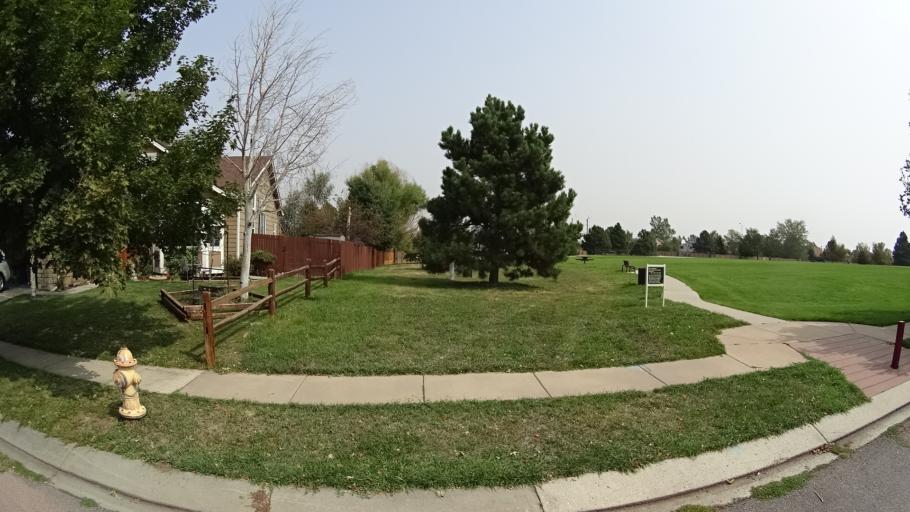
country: US
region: Colorado
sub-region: El Paso County
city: Cimarron Hills
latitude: 38.9196
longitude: -104.7395
